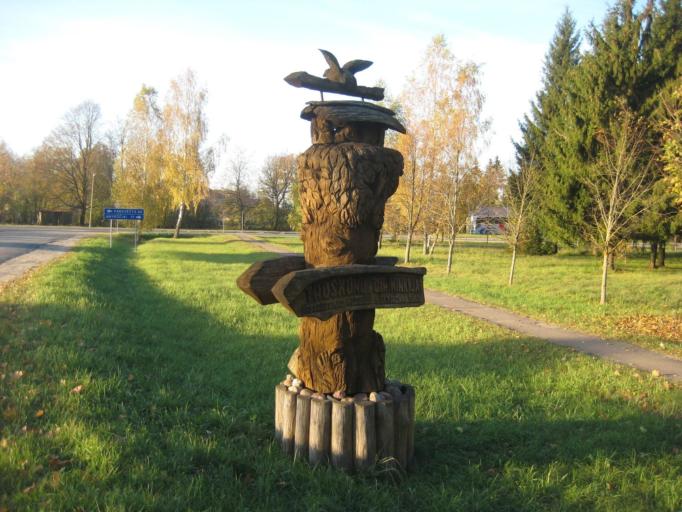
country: LT
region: Utenos apskritis
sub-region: Anyksciai
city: Anyksciai
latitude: 55.5846
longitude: 24.8792
